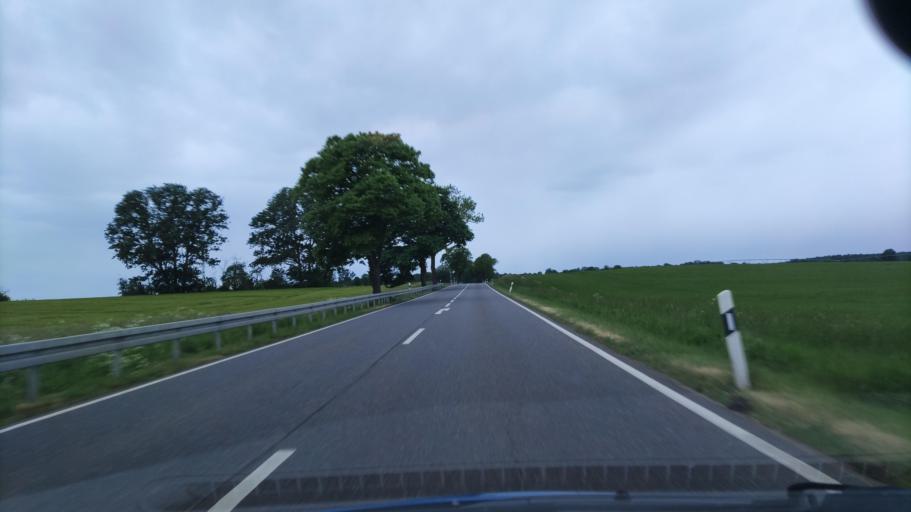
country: DE
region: Mecklenburg-Vorpommern
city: Neuburg
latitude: 53.4425
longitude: 11.8954
